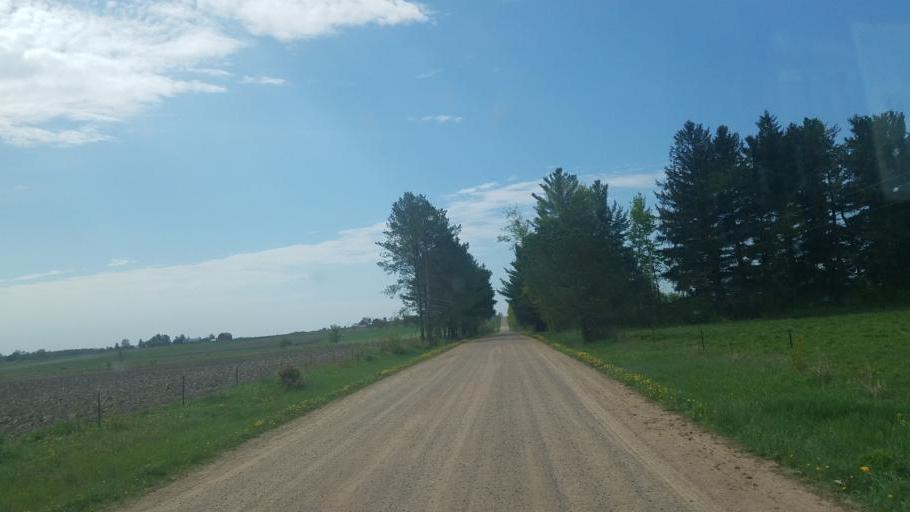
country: US
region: Wisconsin
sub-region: Marathon County
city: Spencer
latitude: 44.6082
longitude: -90.3766
